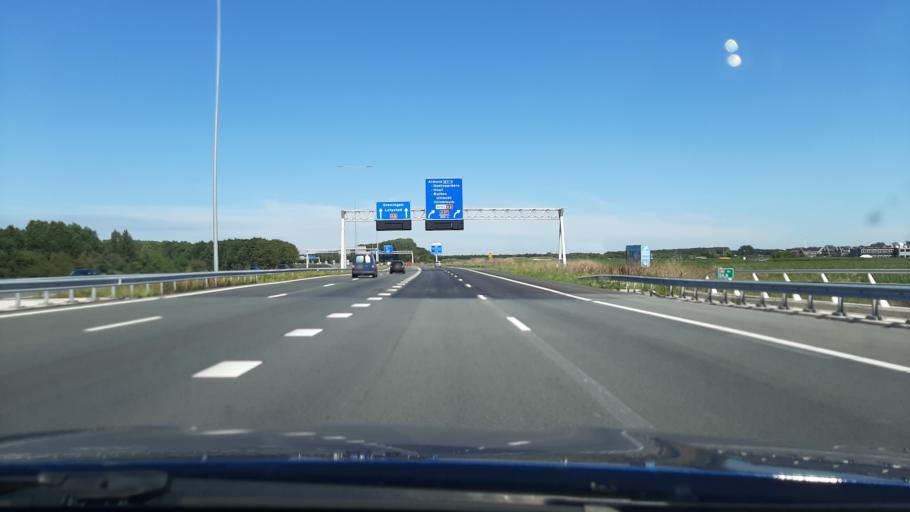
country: NL
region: Flevoland
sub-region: Gemeente Almere
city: Almere Stad
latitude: 52.3607
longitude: 5.2746
